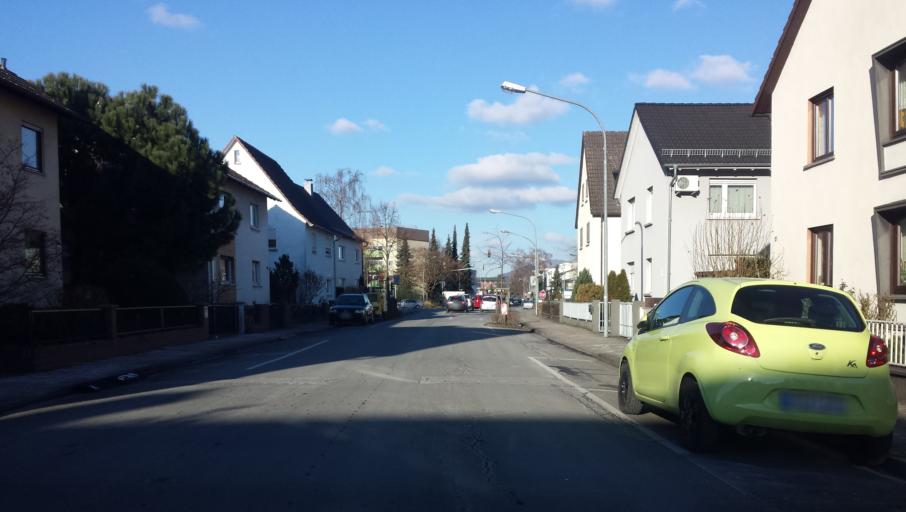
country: DE
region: Hesse
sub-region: Regierungsbezirk Darmstadt
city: Heppenheim an der Bergstrasse
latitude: 49.6417
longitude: 8.6296
